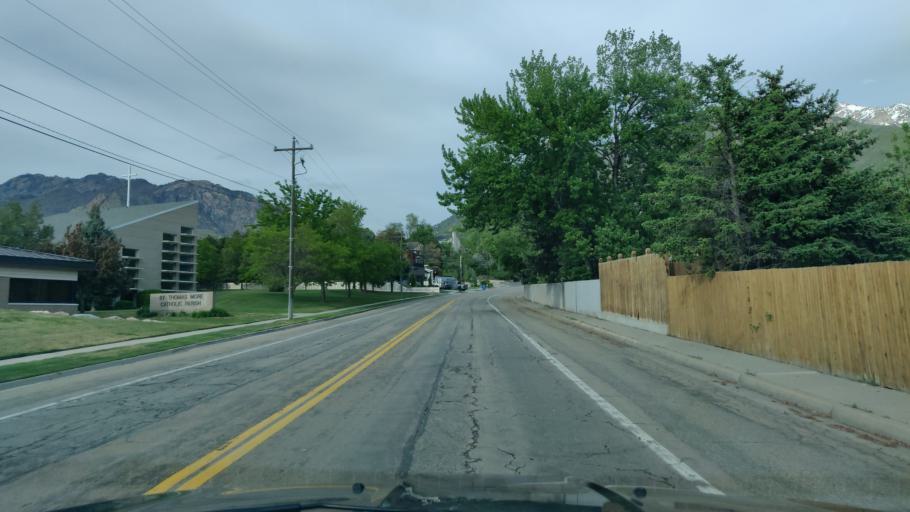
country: US
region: Utah
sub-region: Salt Lake County
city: Cottonwood Heights
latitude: 40.6042
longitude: -111.8081
